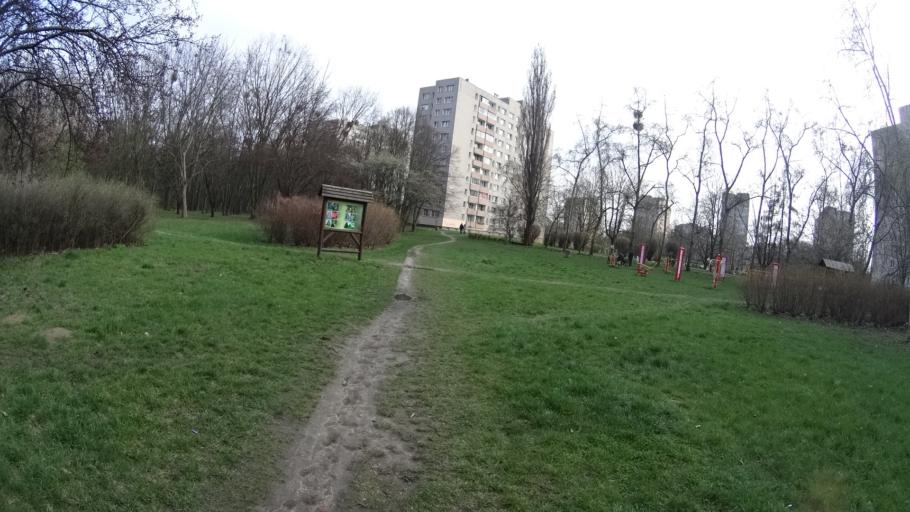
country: PL
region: Masovian Voivodeship
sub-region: Warszawa
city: Bemowo
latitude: 52.2259
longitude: 20.9201
